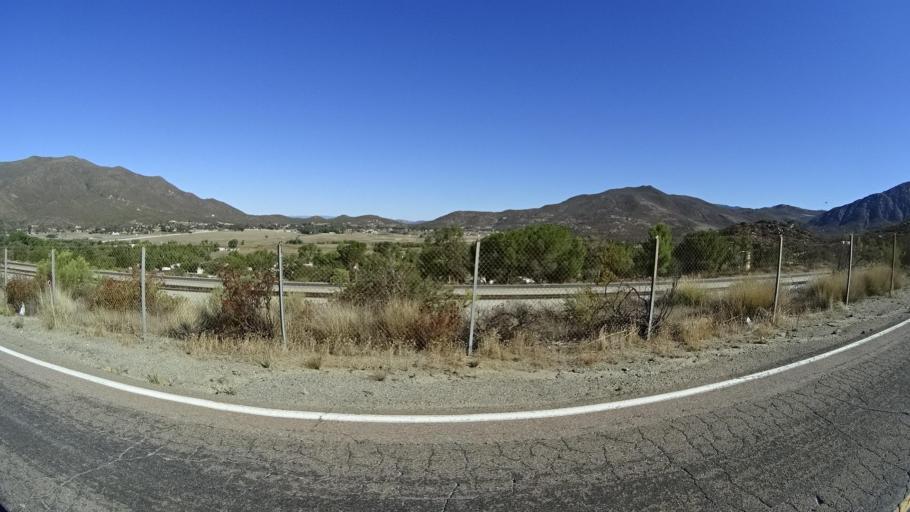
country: US
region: California
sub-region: San Diego County
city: Alpine
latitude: 32.8383
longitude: -116.6934
